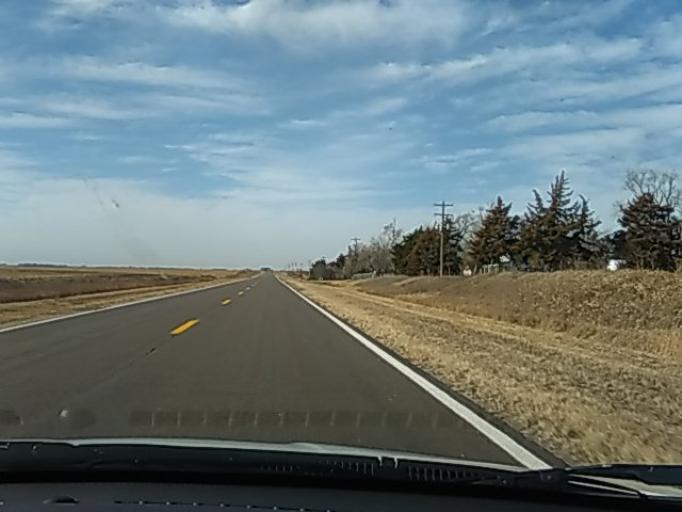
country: US
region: Nebraska
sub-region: Clay County
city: Clay Center
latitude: 40.4232
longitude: -97.9638
